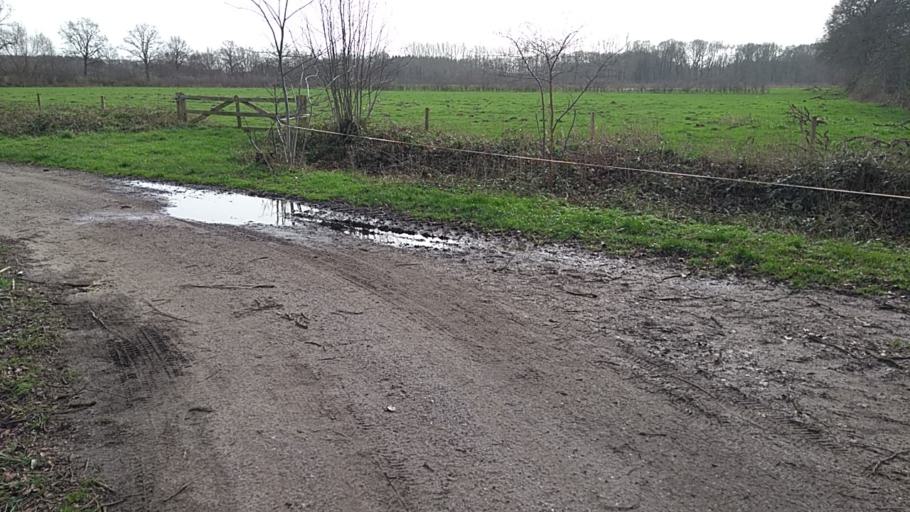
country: NL
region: Overijssel
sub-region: Gemeente Deventer
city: Schalkhaar
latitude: 52.2595
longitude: 6.2466
